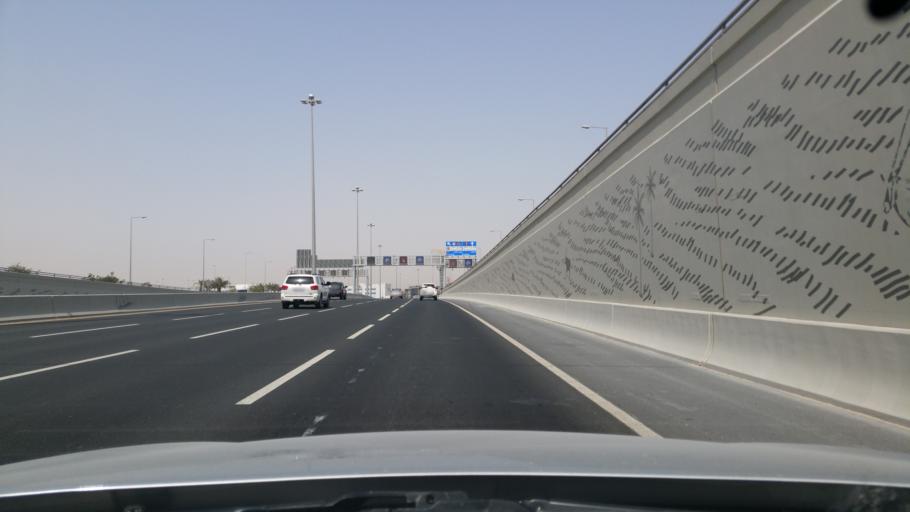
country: QA
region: Baladiyat ar Rayyan
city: Ar Rayyan
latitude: 25.3018
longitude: 51.4282
